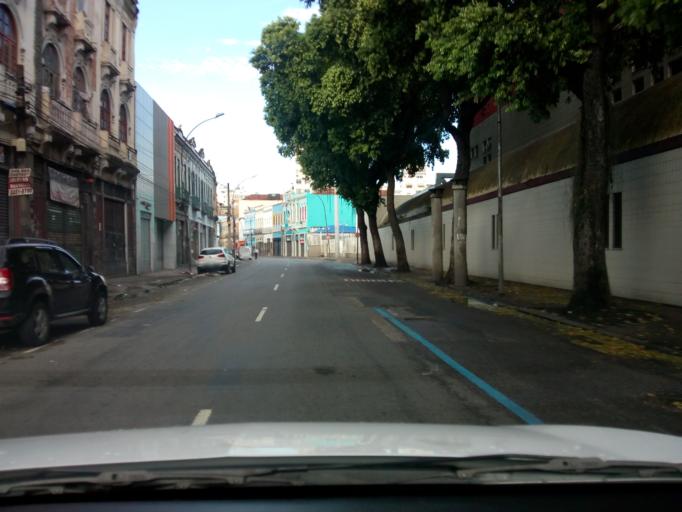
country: BR
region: Rio de Janeiro
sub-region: Rio De Janeiro
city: Rio de Janeiro
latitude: -22.9093
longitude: -43.1897
